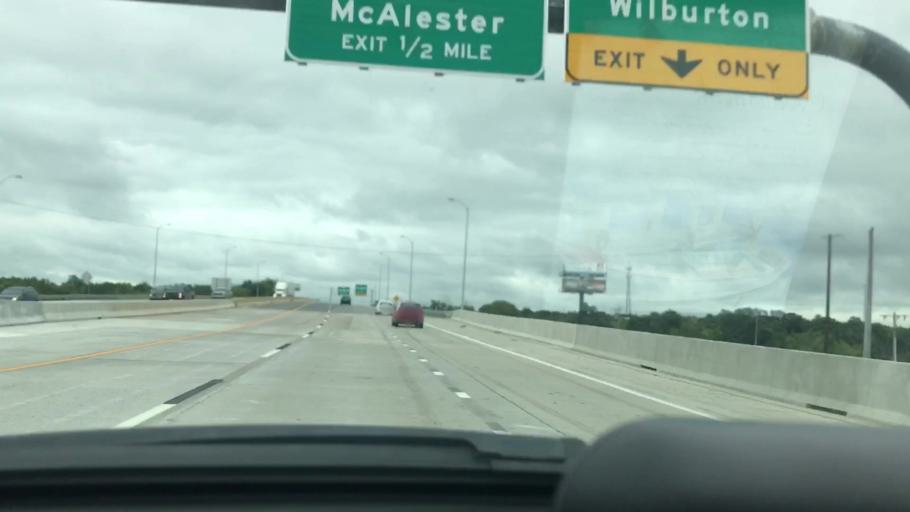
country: US
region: Oklahoma
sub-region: Pittsburg County
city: McAlester
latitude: 34.9217
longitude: -95.7438
